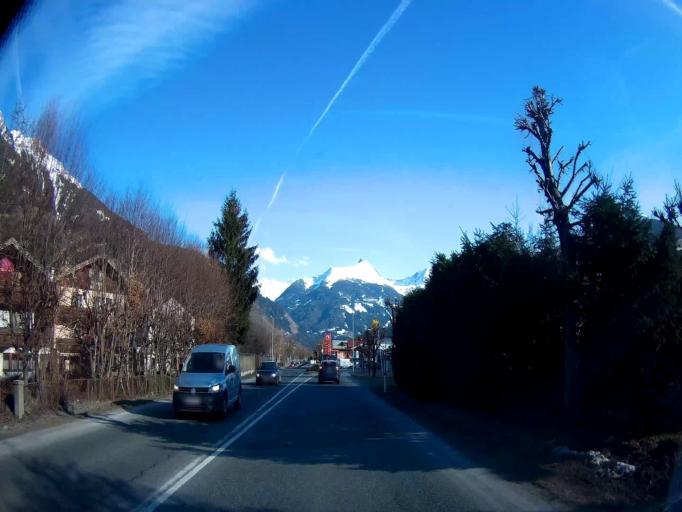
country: AT
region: Salzburg
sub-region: Politischer Bezirk Sankt Johann im Pongau
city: Bad Hofgastein
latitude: 47.1583
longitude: 13.1063
